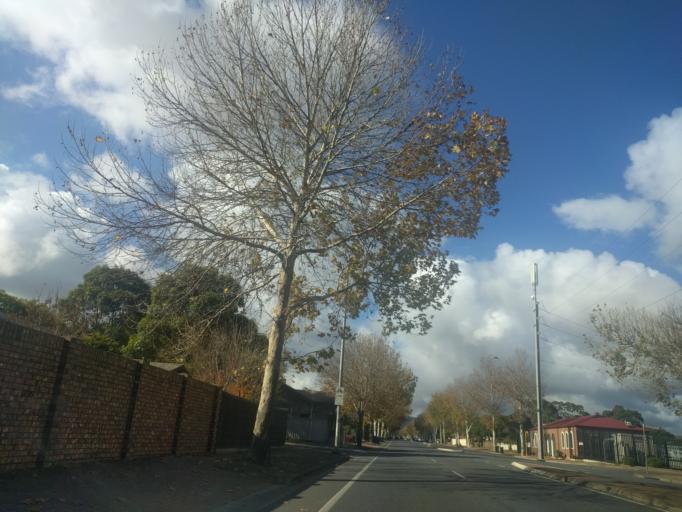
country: AU
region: South Australia
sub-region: Mitcham
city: Clarence Gardens
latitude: -34.9670
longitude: 138.5758
